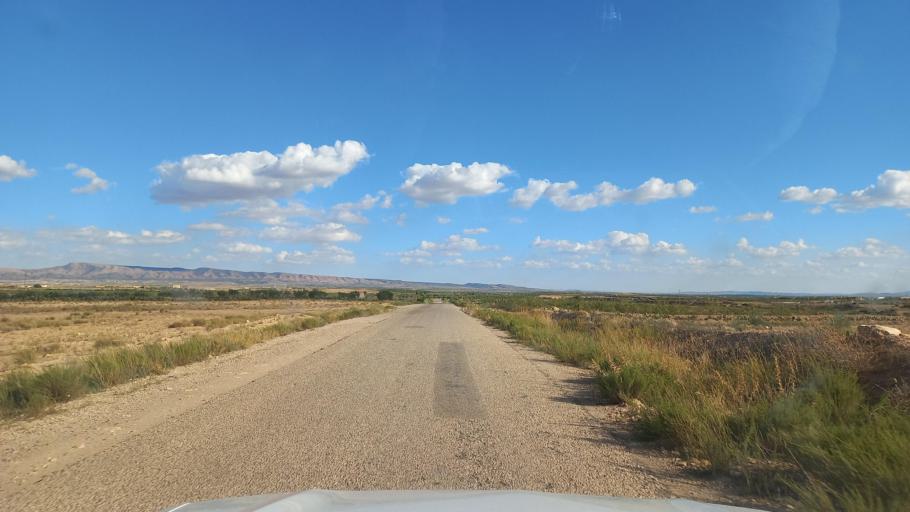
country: TN
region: Al Qasrayn
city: Sbiba
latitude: 35.3902
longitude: 9.0264
